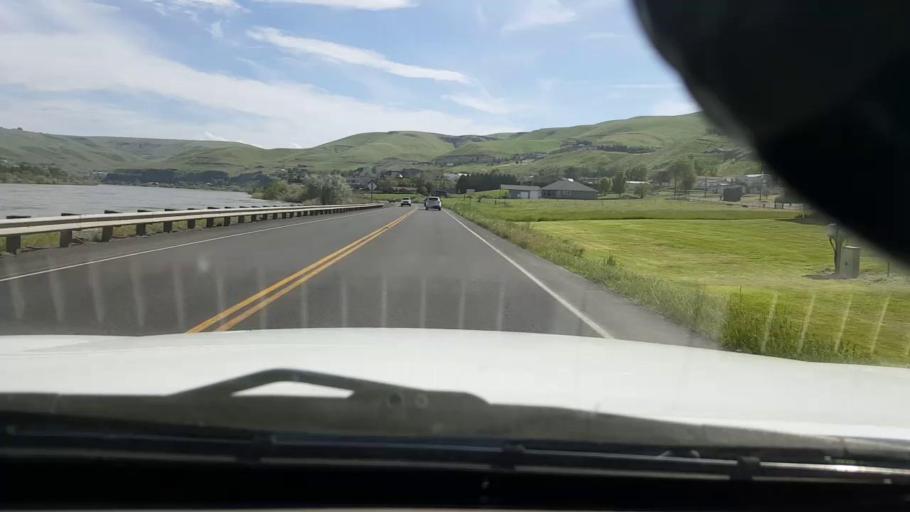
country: US
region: Washington
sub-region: Asotin County
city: Clarkston Heights-Vineland
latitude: 46.3643
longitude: -117.0648
